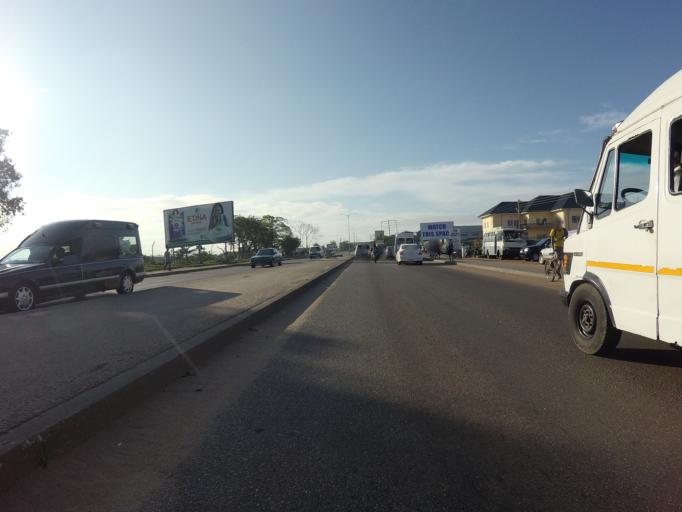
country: GH
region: Greater Accra
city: Accra
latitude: 5.5532
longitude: -0.2311
